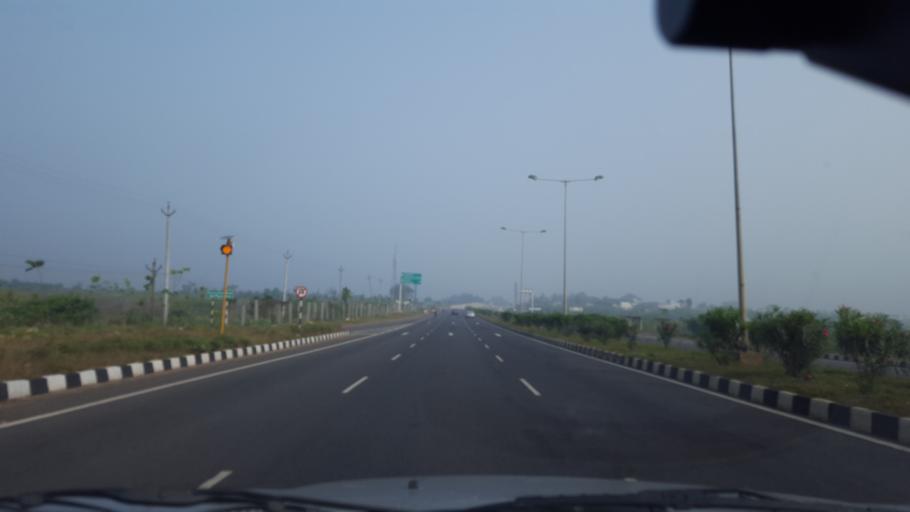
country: IN
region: Andhra Pradesh
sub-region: Prakasam
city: Ongole
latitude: 15.4159
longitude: 80.0391
